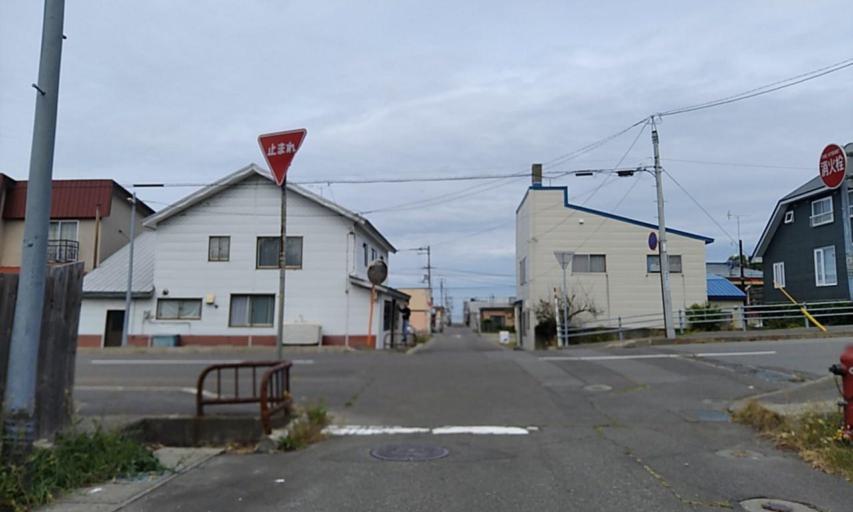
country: JP
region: Hokkaido
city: Rumoi
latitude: 43.8564
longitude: 141.5237
